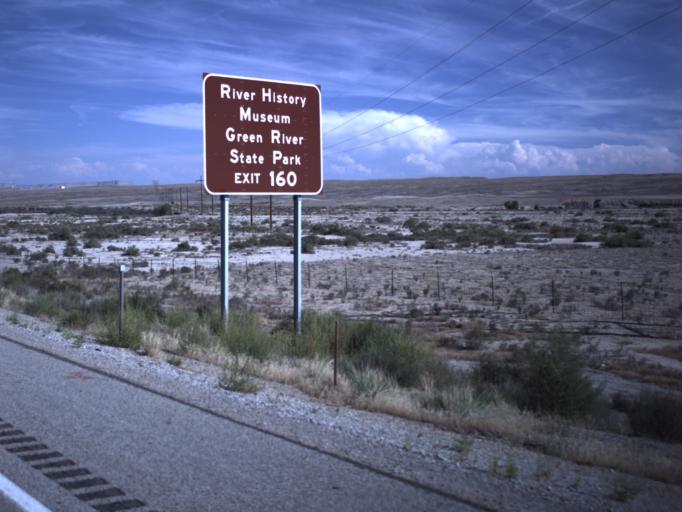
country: US
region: Utah
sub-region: Carbon County
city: East Carbon City
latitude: 38.9870
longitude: -110.2076
